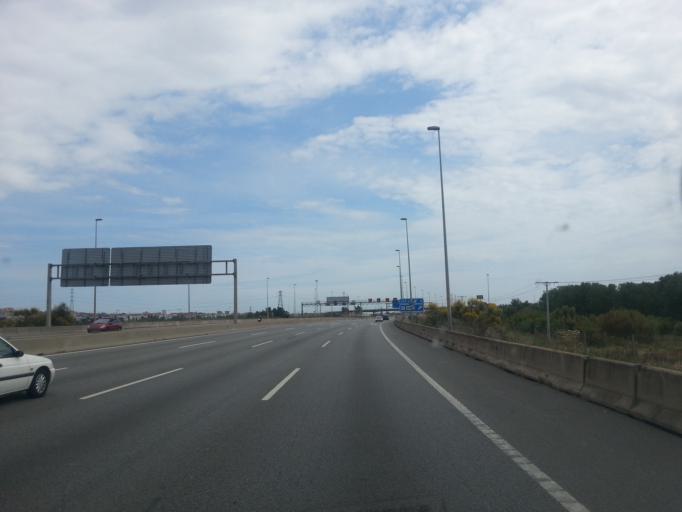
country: ES
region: Catalonia
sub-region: Provincia de Barcelona
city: Sant Vicenc dels Horts
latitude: 41.3981
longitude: 2.0218
